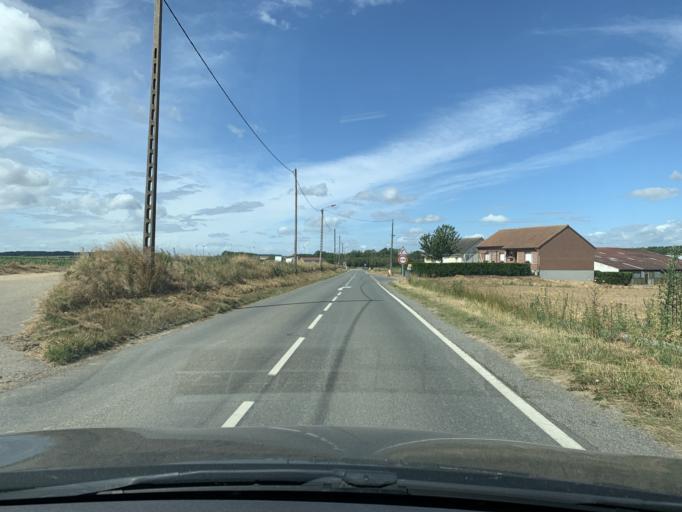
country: FR
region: Nord-Pas-de-Calais
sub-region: Departement du Nord
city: Proville
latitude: 50.1561
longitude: 3.1970
